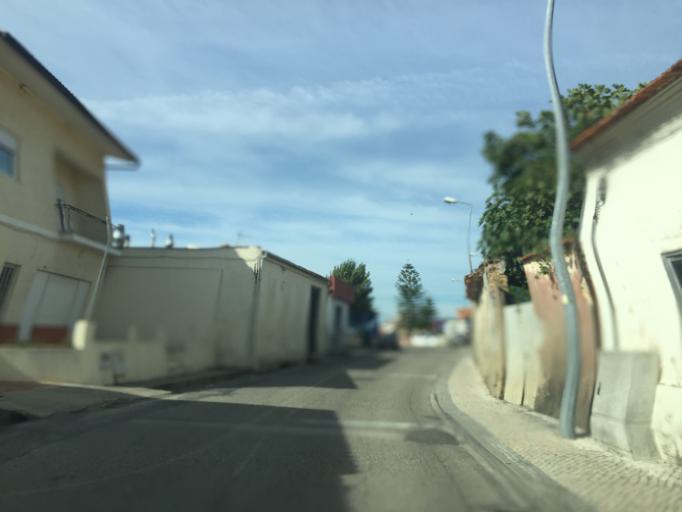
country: PT
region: Coimbra
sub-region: Figueira da Foz
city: Lavos
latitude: 40.0698
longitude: -8.8093
